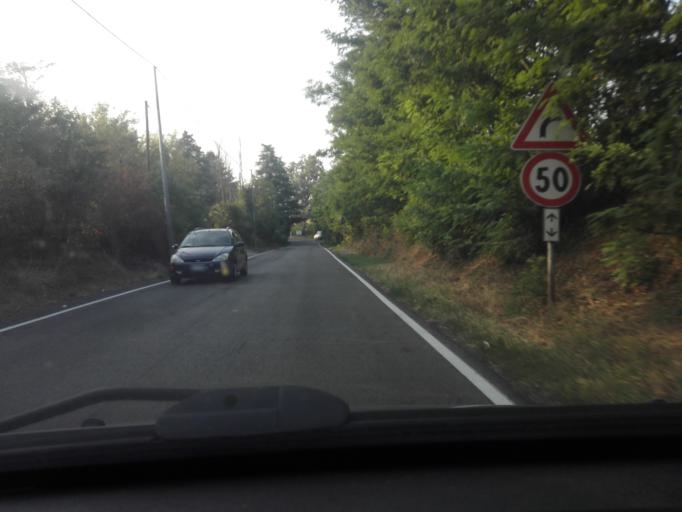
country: IT
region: Piedmont
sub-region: Provincia di Alessandria
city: Villalvernia
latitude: 44.8145
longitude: 8.8540
